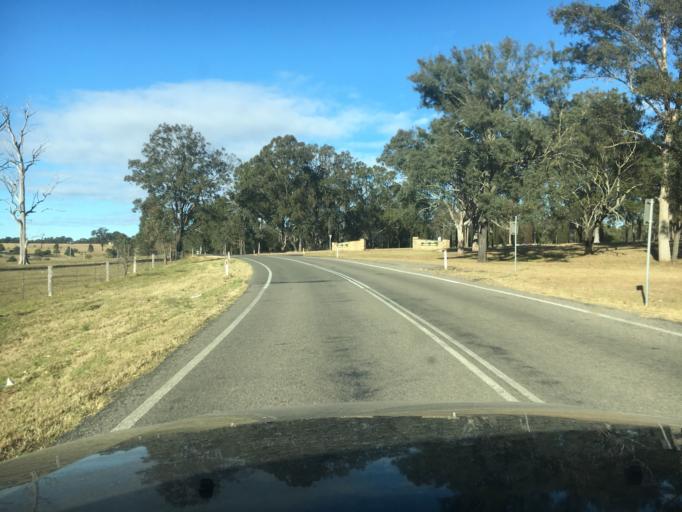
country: AU
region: New South Wales
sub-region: Singleton
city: Singleton
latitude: -32.5464
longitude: 151.2203
